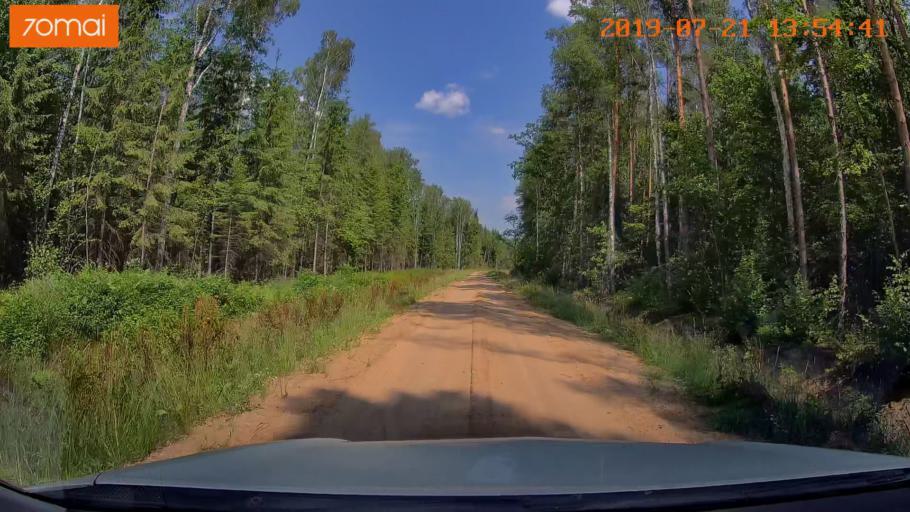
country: BY
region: Grodnenskaya
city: Lyubcha
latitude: 53.7770
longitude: 26.0767
